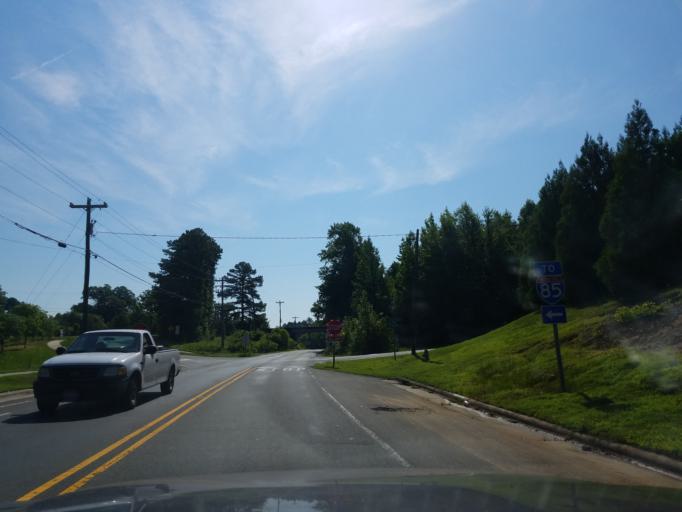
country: US
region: North Carolina
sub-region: Durham County
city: Gorman
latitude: 36.0267
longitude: -78.8416
